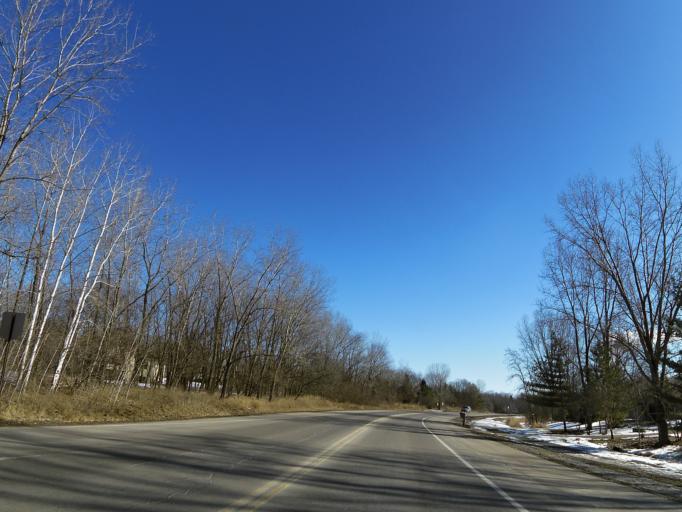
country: US
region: Minnesota
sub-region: Washington County
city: Stillwater
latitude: 45.0566
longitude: -92.8313
